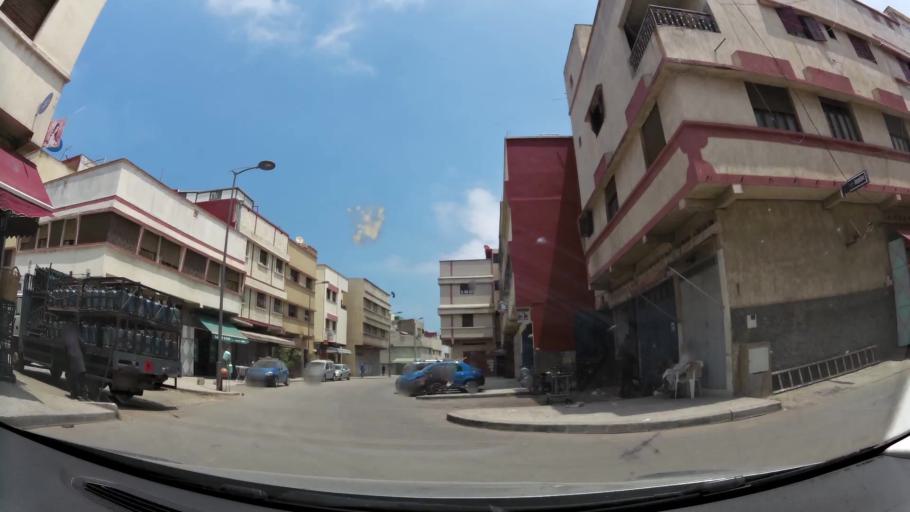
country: MA
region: Rabat-Sale-Zemmour-Zaer
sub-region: Skhirate-Temara
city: Temara
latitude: 33.9800
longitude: -6.8856
